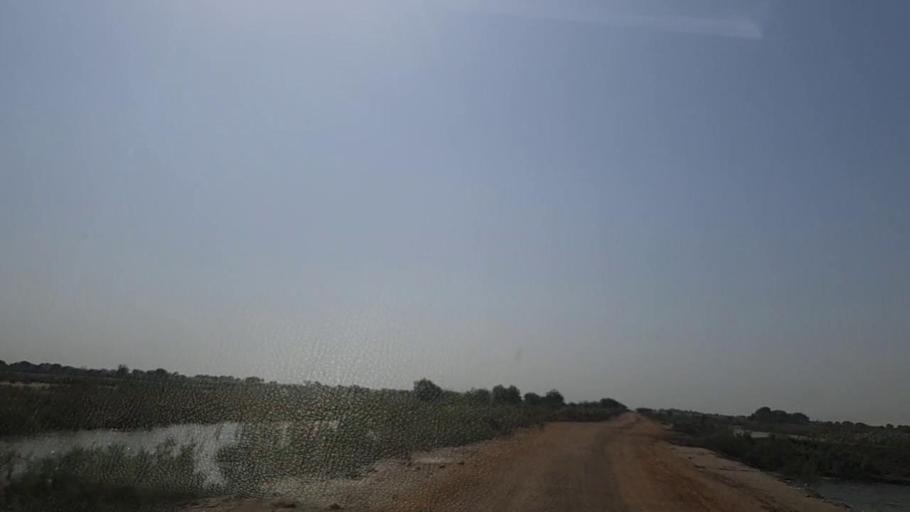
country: PK
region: Sindh
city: Daro Mehar
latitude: 24.7031
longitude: 68.1285
